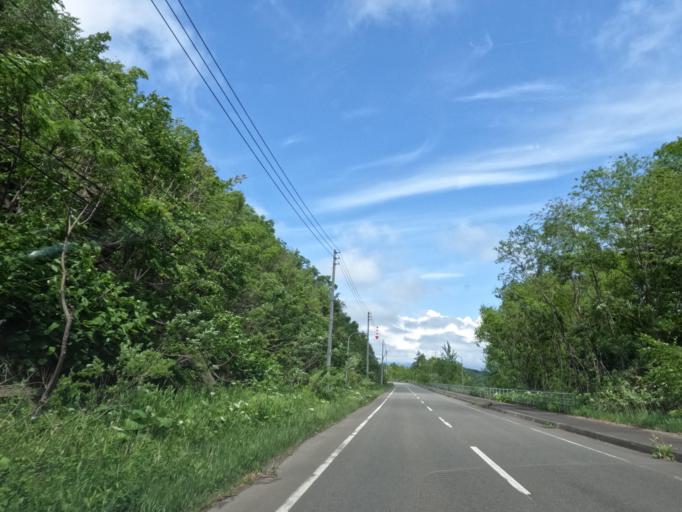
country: JP
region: Hokkaido
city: Tobetsu
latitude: 43.3215
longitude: 141.5685
